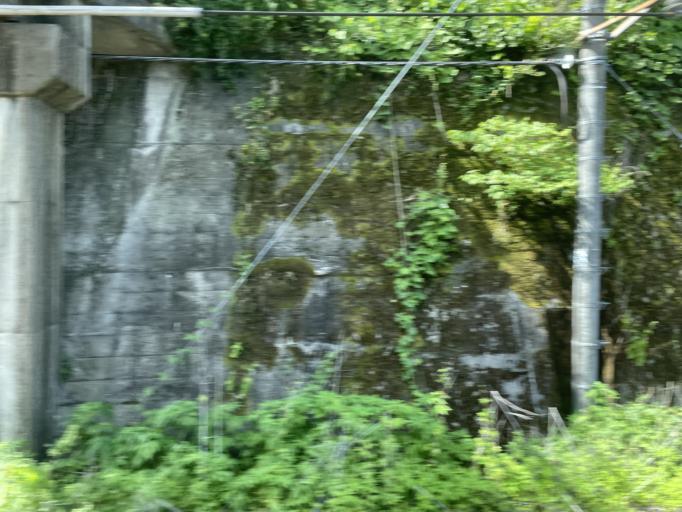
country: JP
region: Yamanashi
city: Otsuki
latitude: 35.6139
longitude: 138.9730
